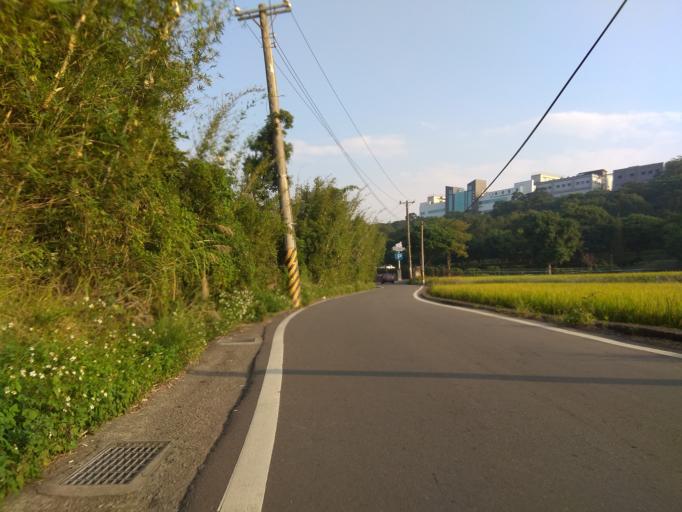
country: TW
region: Taiwan
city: Daxi
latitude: 24.9083
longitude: 121.1969
